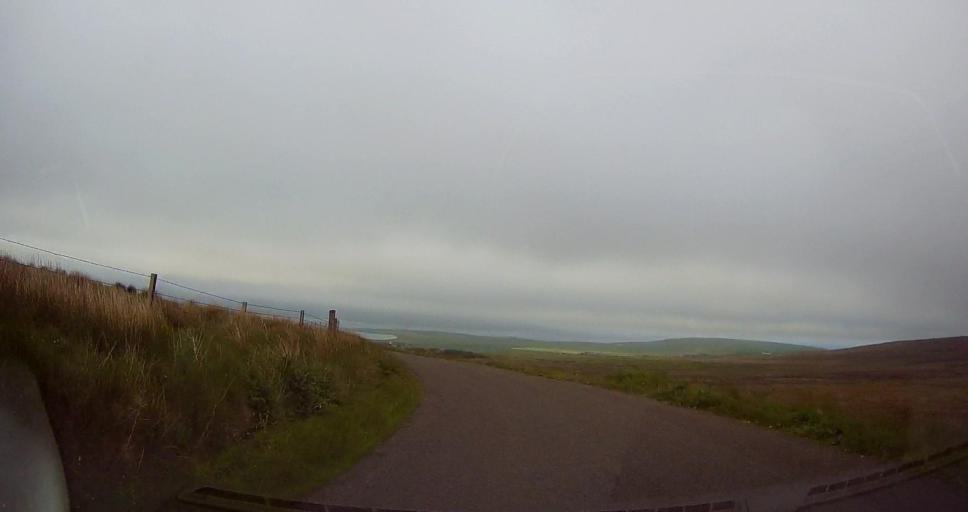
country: GB
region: Scotland
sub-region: Orkney Islands
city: Orkney
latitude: 59.1051
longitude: -3.1293
